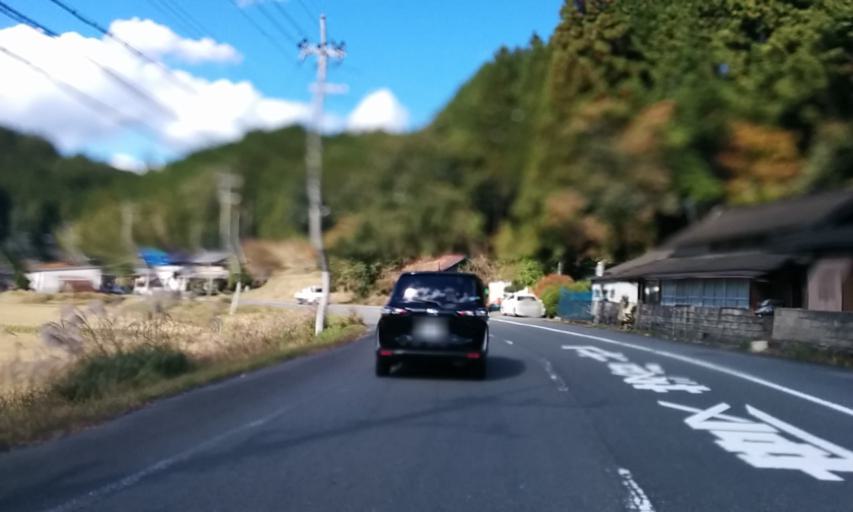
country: JP
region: Kyoto
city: Kameoka
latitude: 35.2094
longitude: 135.5730
